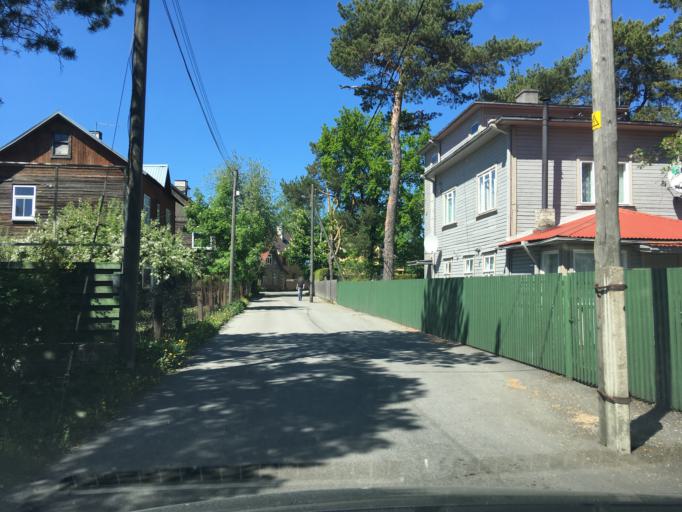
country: EE
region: Harju
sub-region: Saue vald
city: Laagri
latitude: 59.3863
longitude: 24.6758
